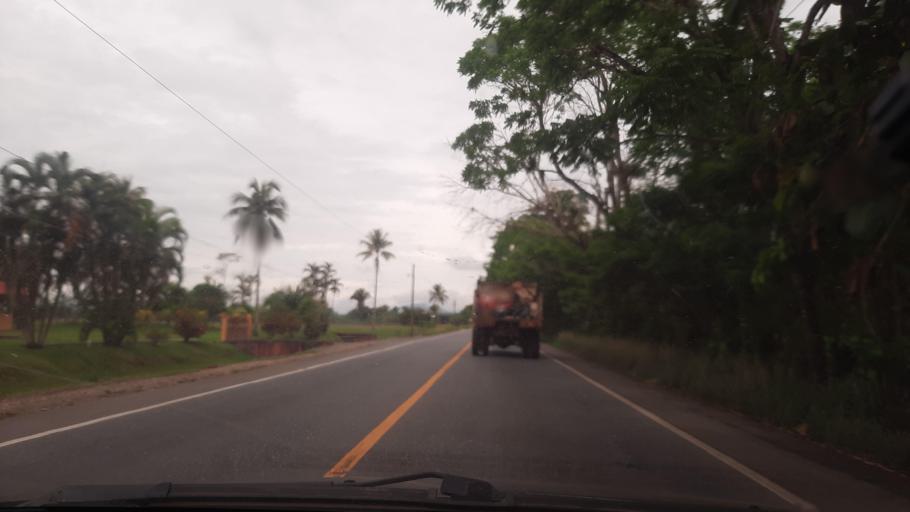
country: GT
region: Izabal
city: Morales
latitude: 15.4709
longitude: -88.9019
